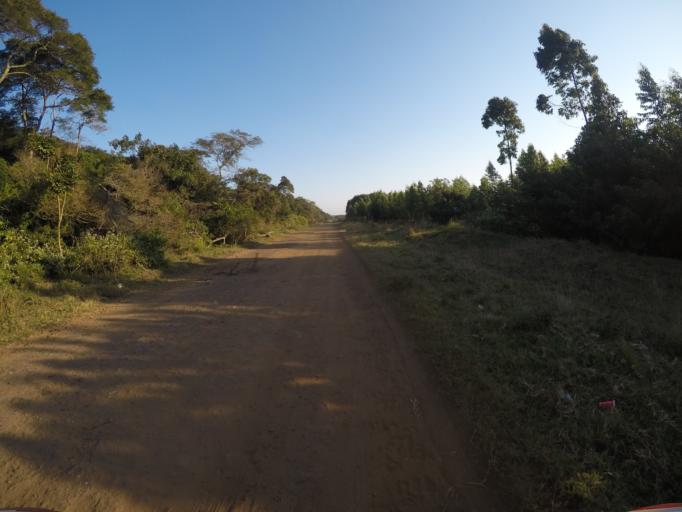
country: ZA
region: KwaZulu-Natal
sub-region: uThungulu District Municipality
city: KwaMbonambi
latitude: -28.6958
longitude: 32.1966
